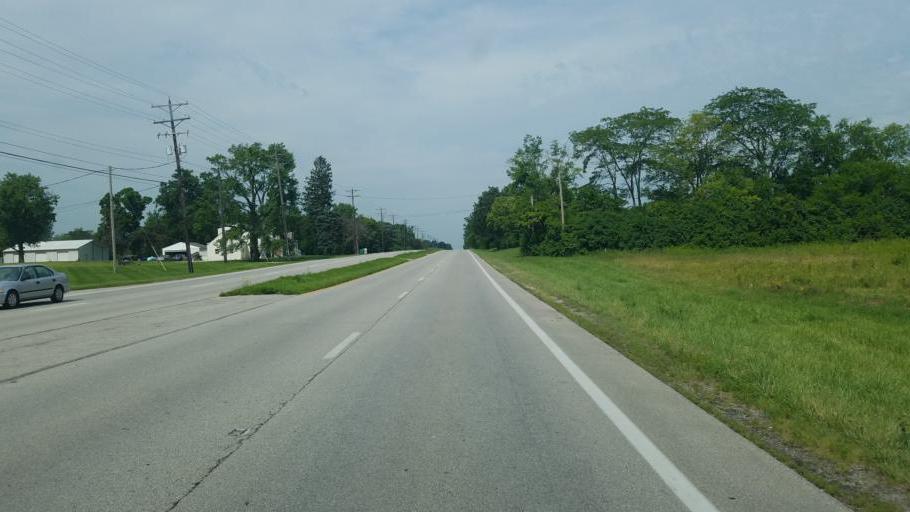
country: US
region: Ohio
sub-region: Franklin County
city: Lake Darby
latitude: 39.9498
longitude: -83.1855
